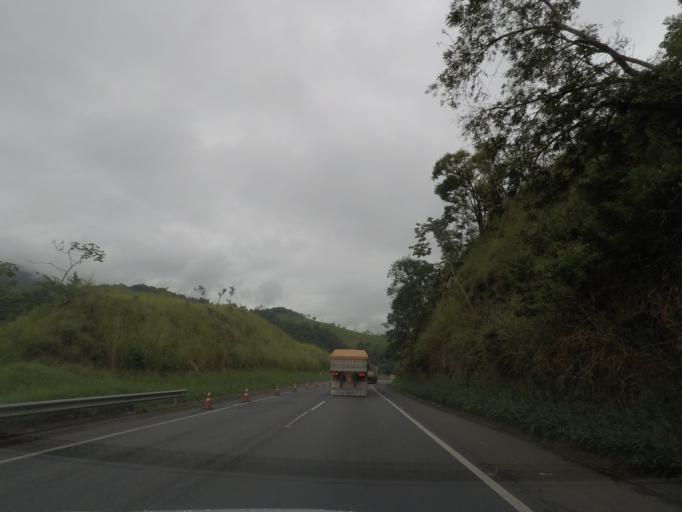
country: BR
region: Sao Paulo
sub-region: Cajati
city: Cajati
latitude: -24.8209
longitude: -48.2105
